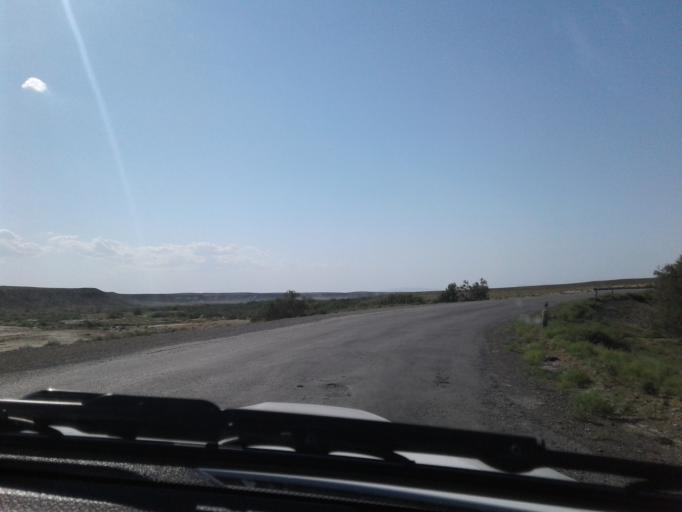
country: TM
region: Balkan
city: Serdar
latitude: 38.7139
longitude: 56.2938
